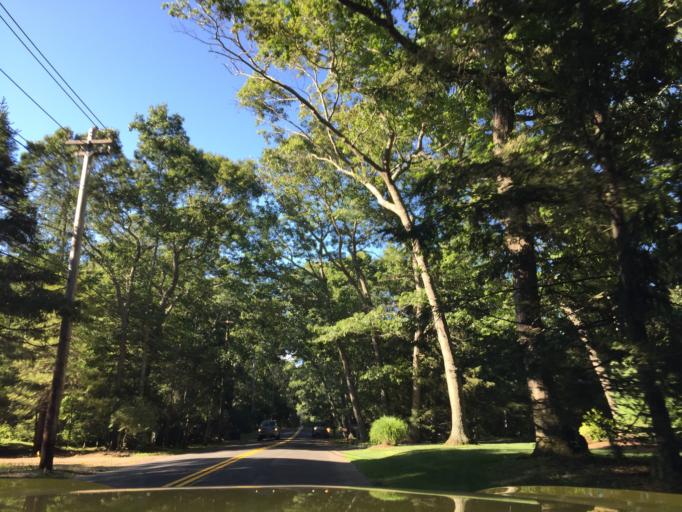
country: US
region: New York
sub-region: Suffolk County
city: Southold
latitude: 41.0469
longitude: -72.4111
